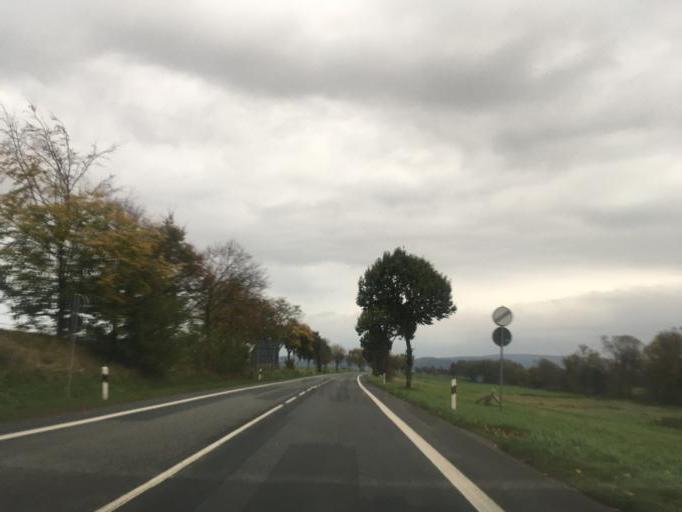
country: DE
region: Lower Saxony
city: Hardegsen
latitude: 51.6417
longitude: 9.8728
